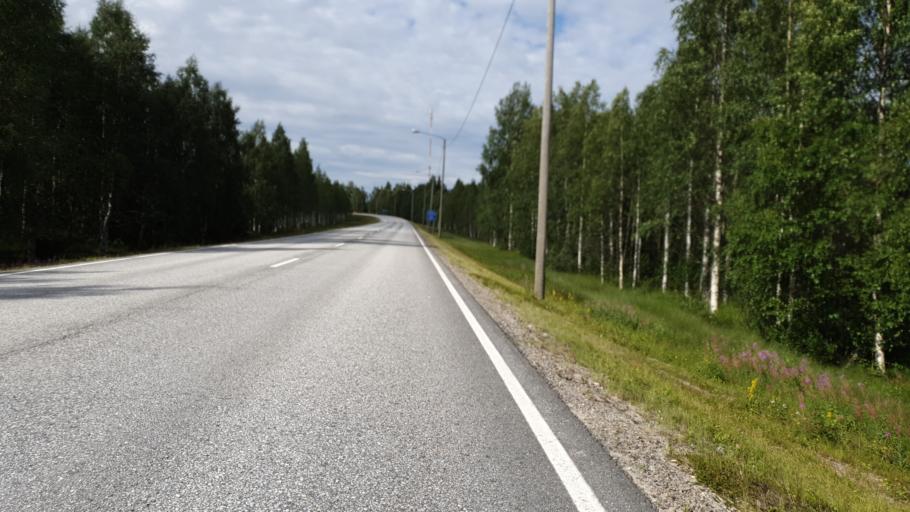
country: FI
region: Kainuu
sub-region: Kehys-Kainuu
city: Kuhmo
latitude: 64.5409
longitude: 29.9559
